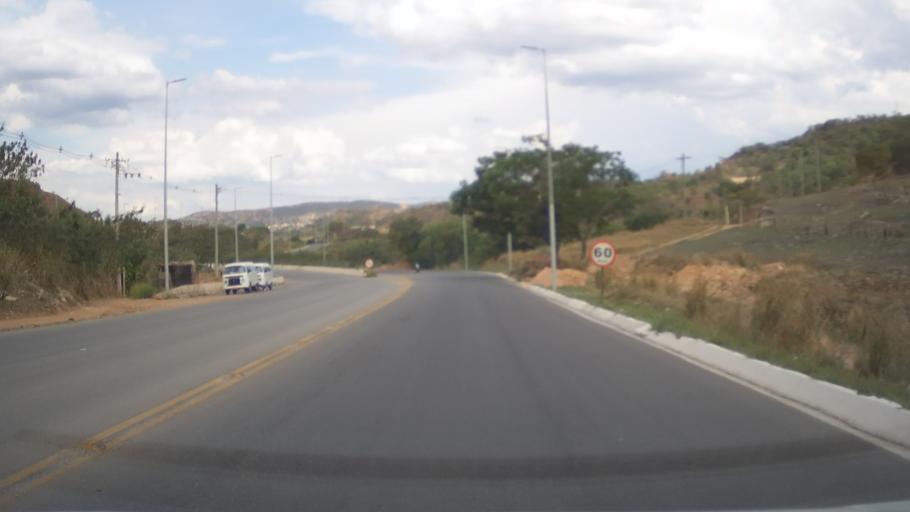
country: BR
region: Minas Gerais
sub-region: Belo Horizonte
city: Belo Horizonte
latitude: -19.8703
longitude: -43.8899
